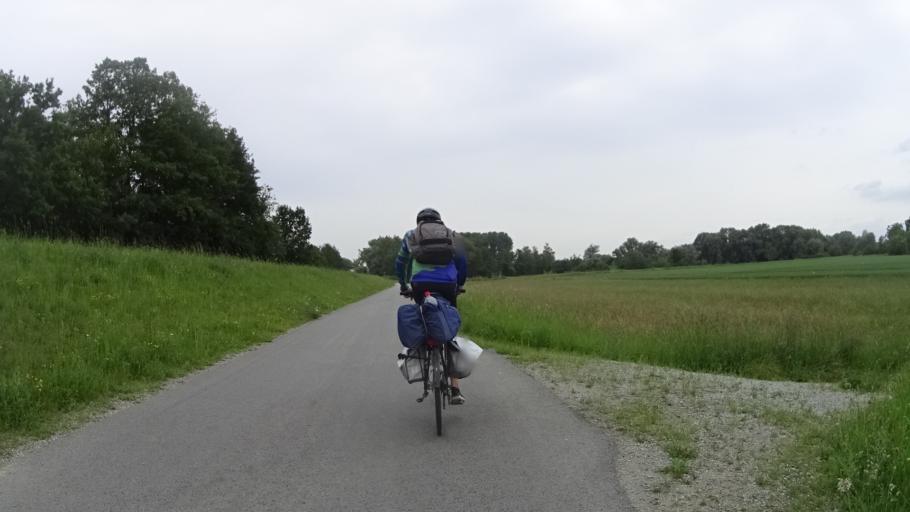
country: DE
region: Bavaria
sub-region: Lower Bavaria
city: Hofkirchen
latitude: 48.6915
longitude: 13.1139
